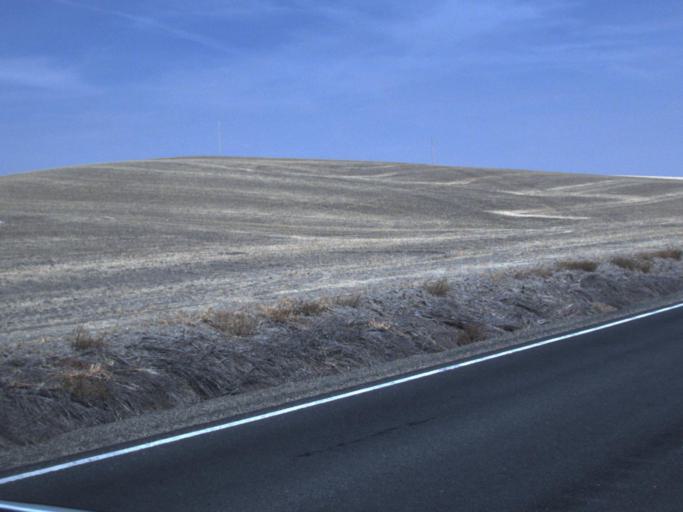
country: US
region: Washington
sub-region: Whitman County
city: Colfax
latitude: 47.1650
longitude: -117.2088
